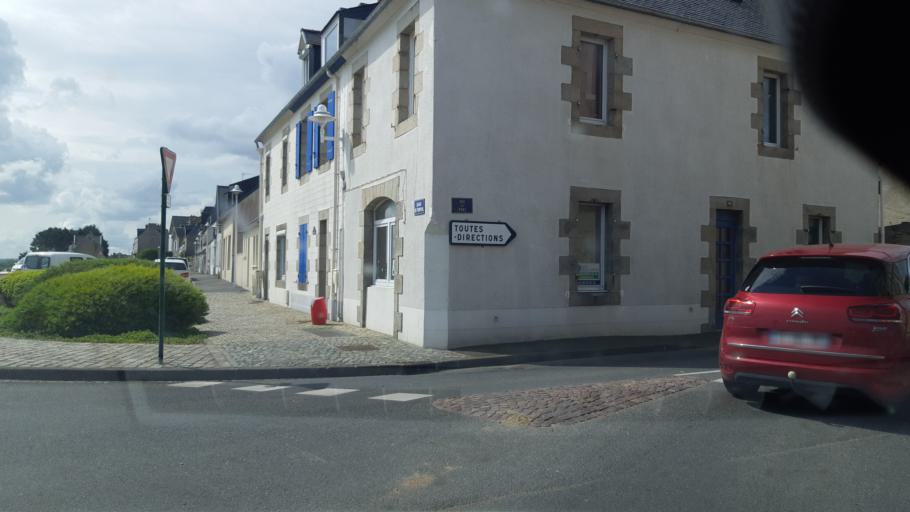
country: FR
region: Brittany
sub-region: Departement du Finistere
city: Saint-Pol-de-Leon
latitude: 48.6827
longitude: -3.9709
